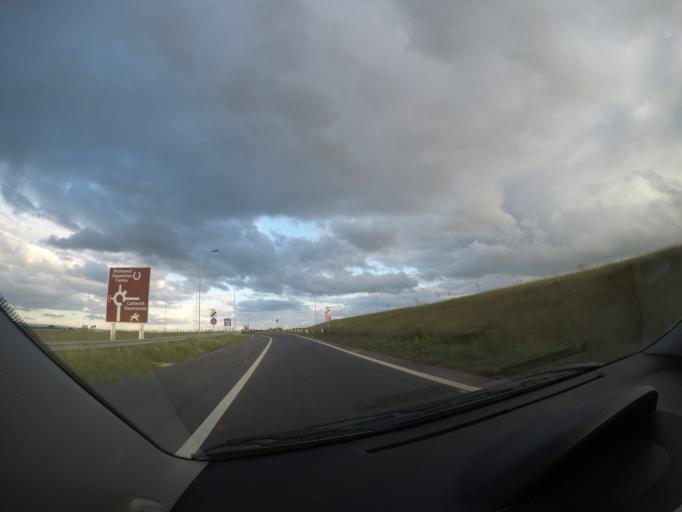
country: GB
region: England
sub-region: North Yorkshire
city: Catterick
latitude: 54.3809
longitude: -1.6516
